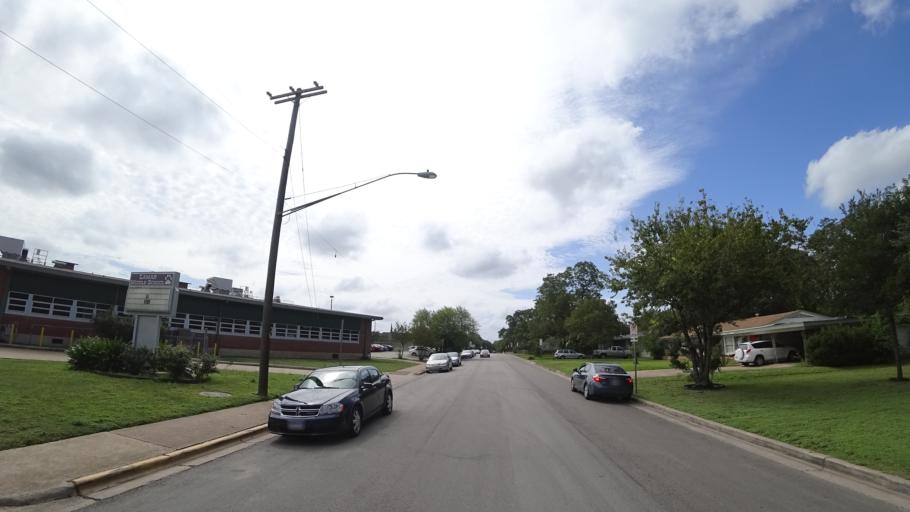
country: US
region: Texas
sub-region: Travis County
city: Austin
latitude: 30.3375
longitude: -97.7413
